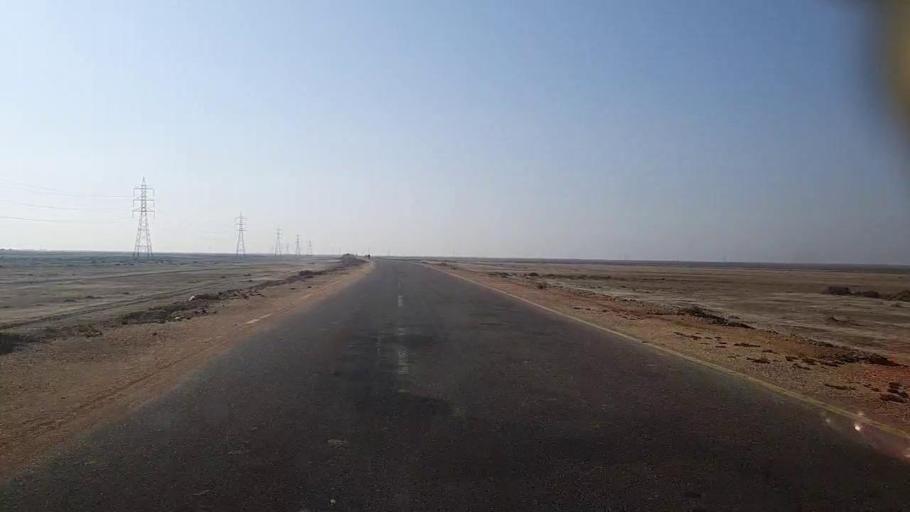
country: PK
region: Sindh
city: Mirpur Sakro
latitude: 24.6108
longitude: 67.4970
